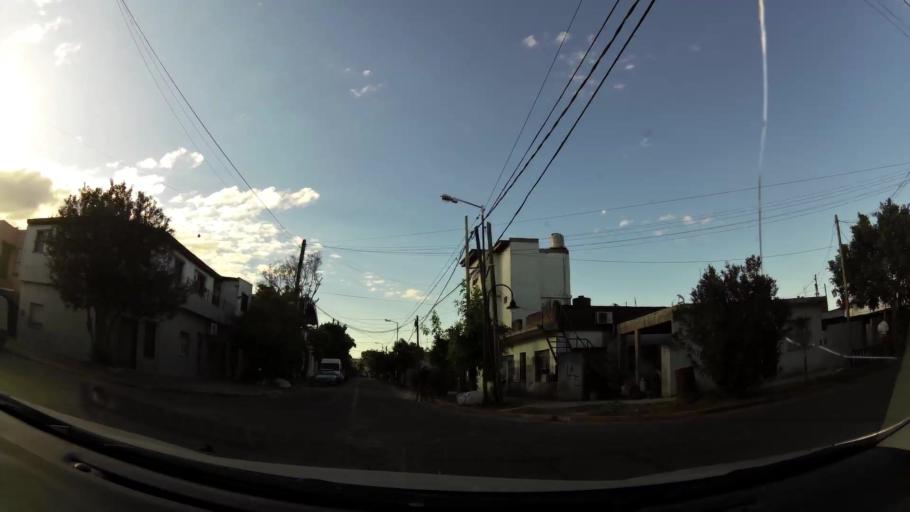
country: AR
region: Buenos Aires
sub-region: Partido de Tigre
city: Tigre
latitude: -34.4566
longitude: -58.5682
